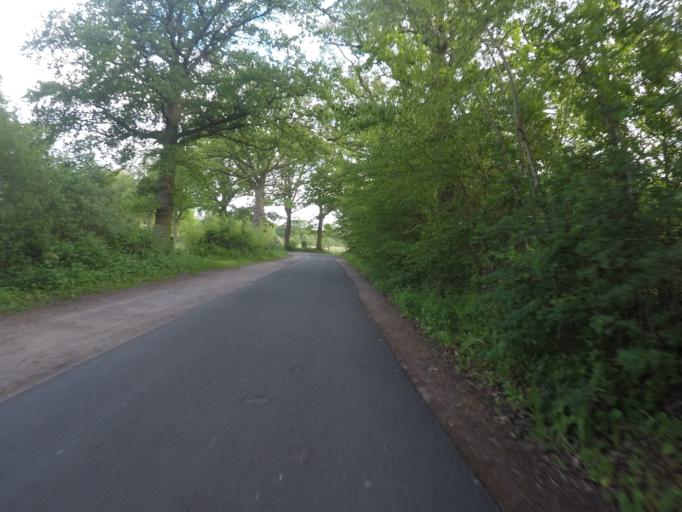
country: DE
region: Schleswig-Holstein
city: Bonningstedt
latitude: 53.6609
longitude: 9.9258
